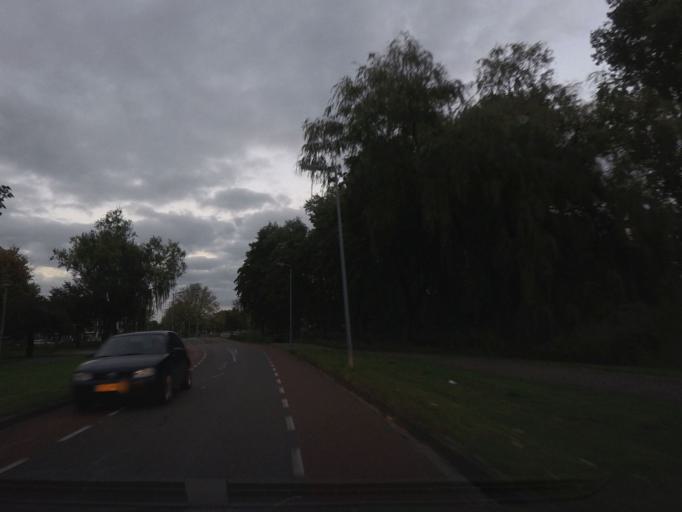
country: NL
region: North Holland
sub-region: Gemeente Alkmaar
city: Alkmaar
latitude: 52.6351
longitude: 4.7303
